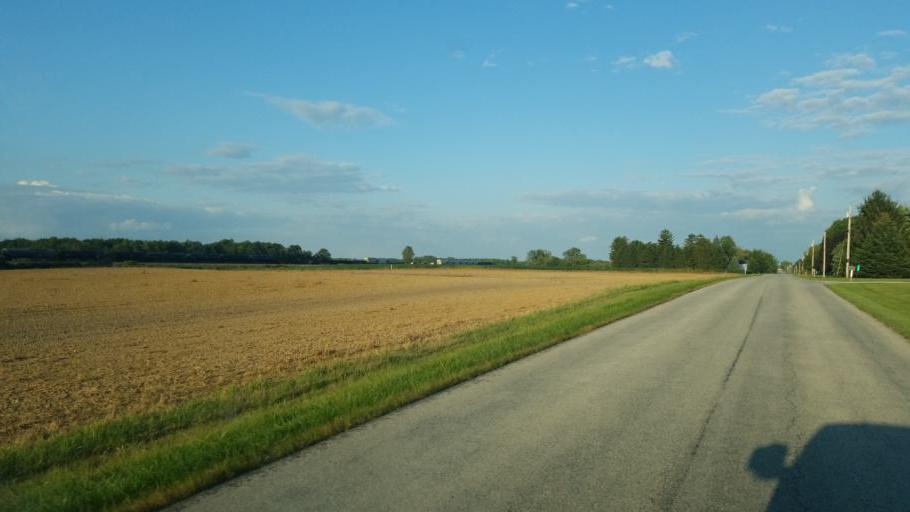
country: US
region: Ohio
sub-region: Huron County
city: Plymouth
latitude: 41.0523
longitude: -82.6557
